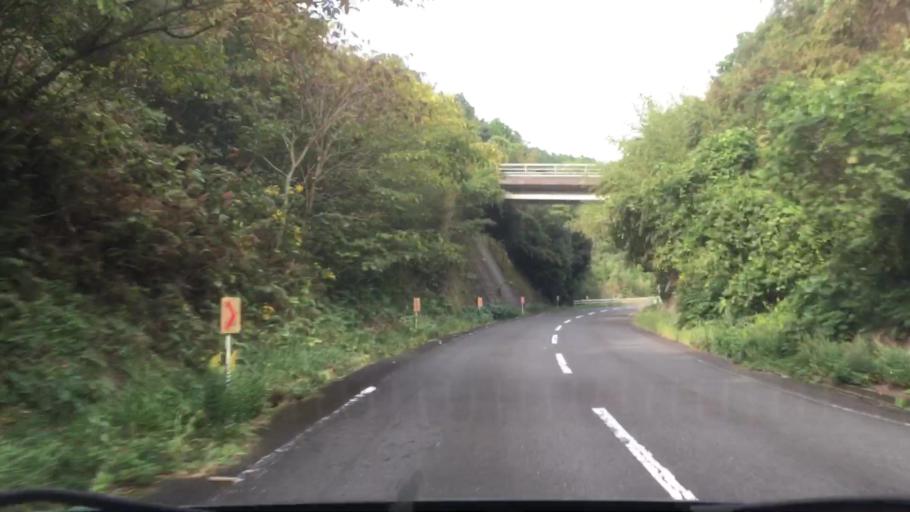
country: JP
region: Nagasaki
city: Sasebo
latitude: 32.9952
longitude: 129.7152
